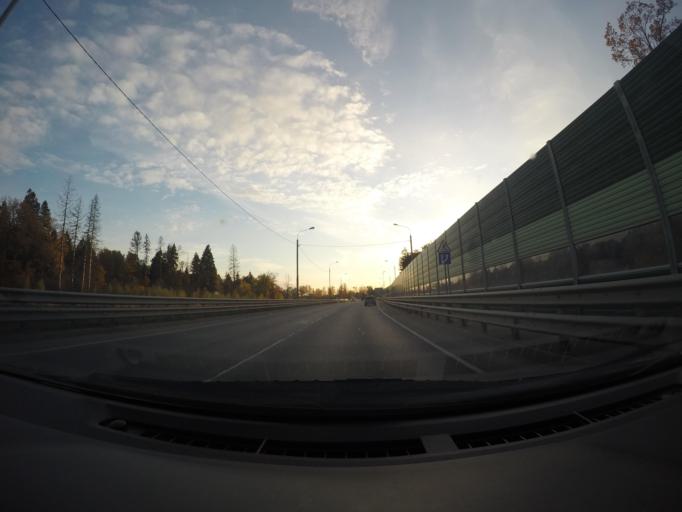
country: RU
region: Moskovskaya
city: Firsanovka
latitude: 55.9512
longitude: 37.2549
